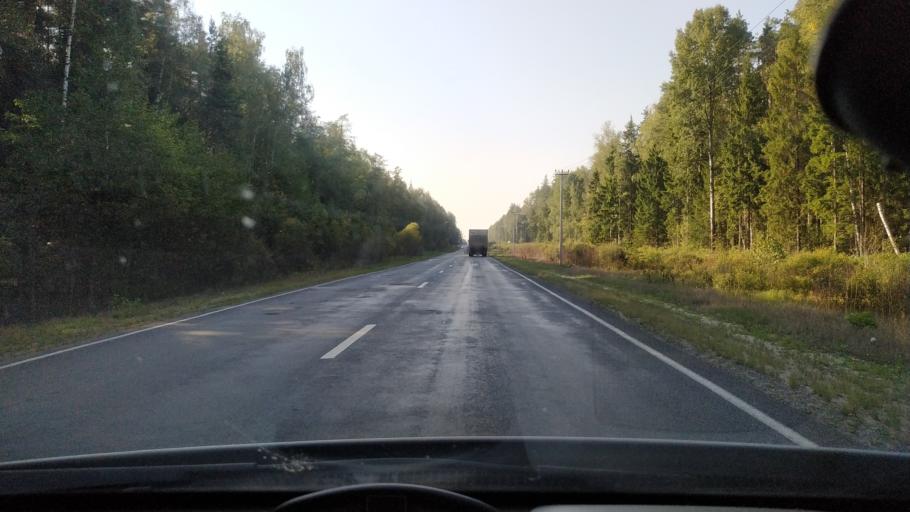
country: RU
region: Moskovskaya
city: Tugolesskiy Bor
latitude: 55.5114
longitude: 39.7123
